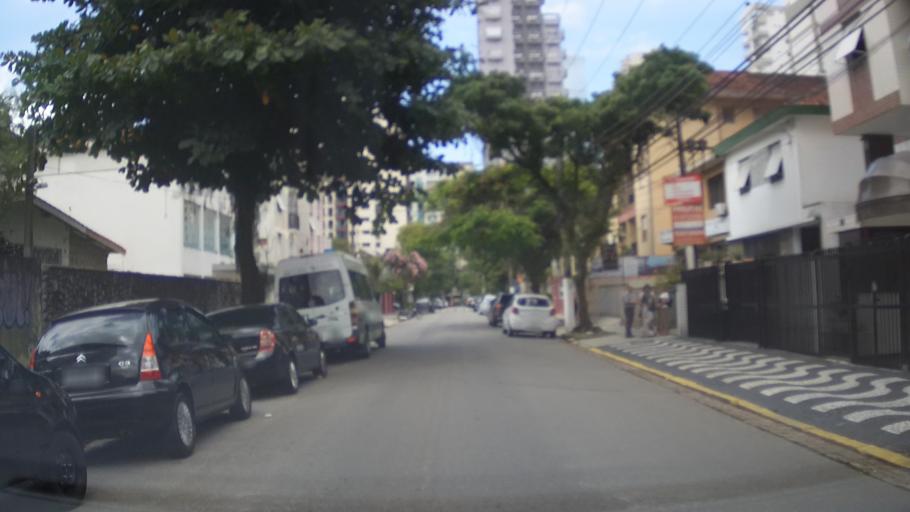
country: BR
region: Sao Paulo
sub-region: Santos
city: Santos
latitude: -23.9643
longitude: -46.3409
